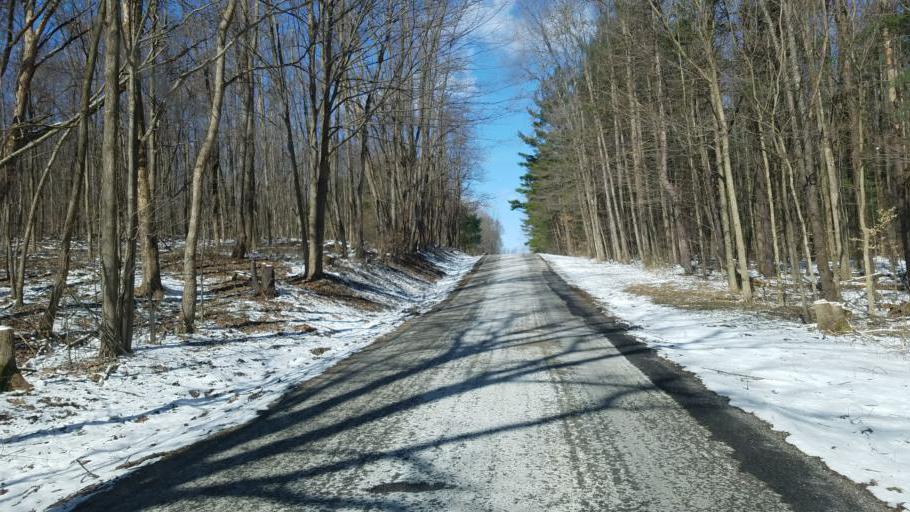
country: US
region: Ohio
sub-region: Richland County
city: Ontario
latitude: 40.7278
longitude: -82.6578
